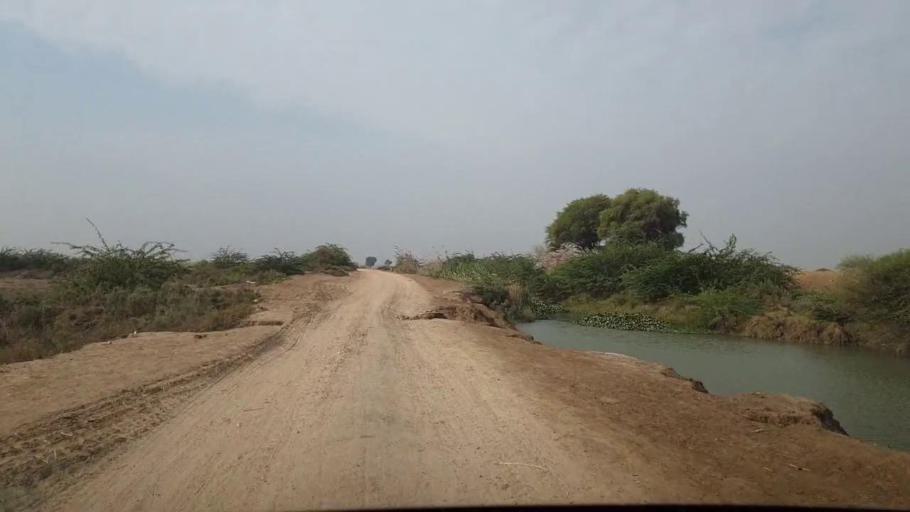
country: PK
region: Sindh
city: Chuhar Jamali
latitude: 24.4041
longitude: 67.9093
